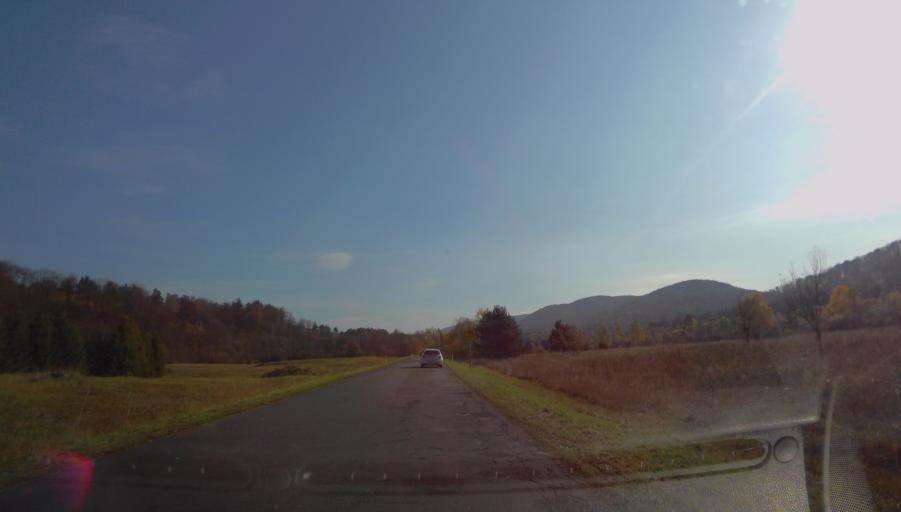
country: PL
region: Subcarpathian Voivodeship
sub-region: Powiat leski
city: Baligrod
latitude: 49.2266
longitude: 22.1743
